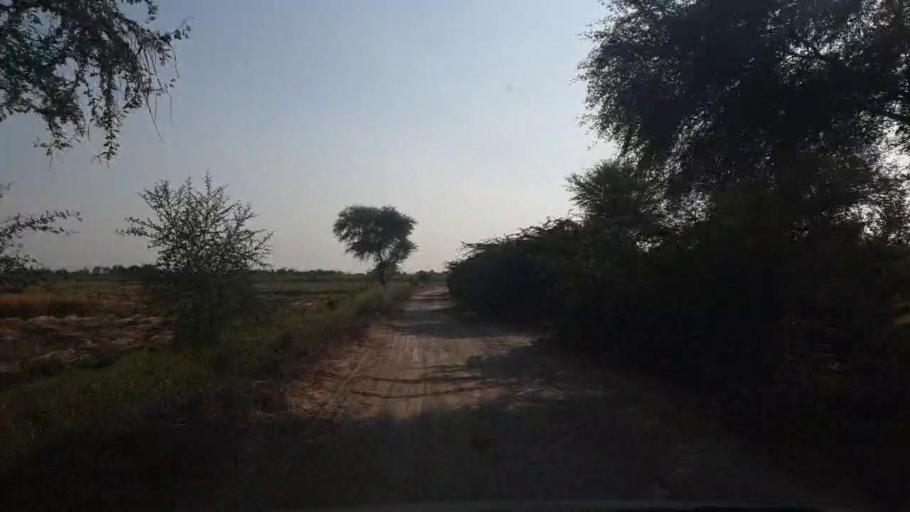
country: PK
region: Sindh
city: Badin
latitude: 24.6346
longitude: 68.7982
